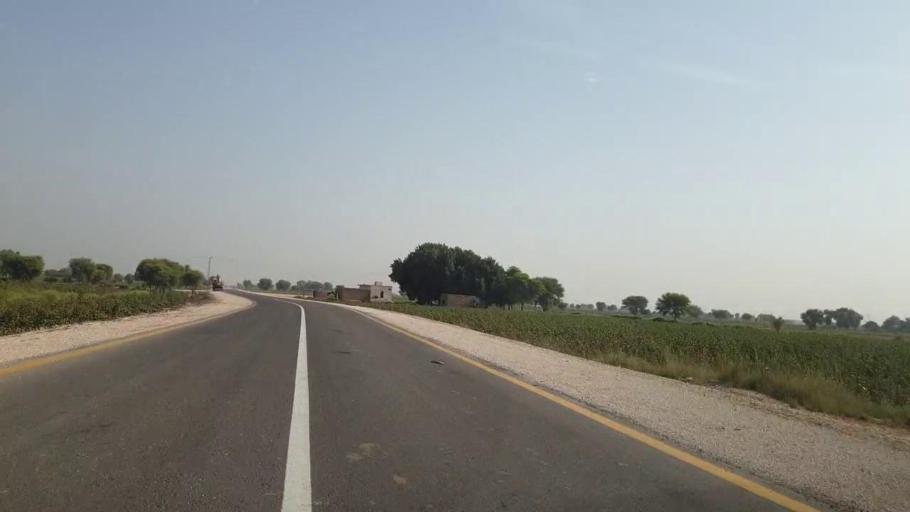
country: PK
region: Sindh
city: Sehwan
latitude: 26.4762
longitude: 67.7865
